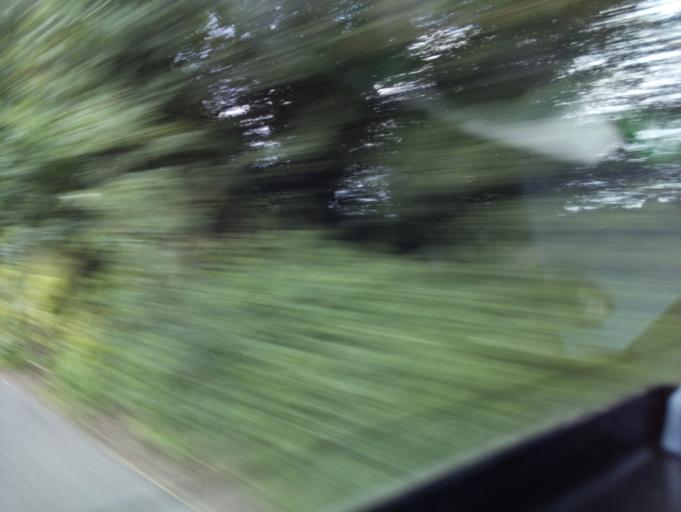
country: GB
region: England
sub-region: Gloucestershire
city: Chipping Campden
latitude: 52.0056
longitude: -1.7612
